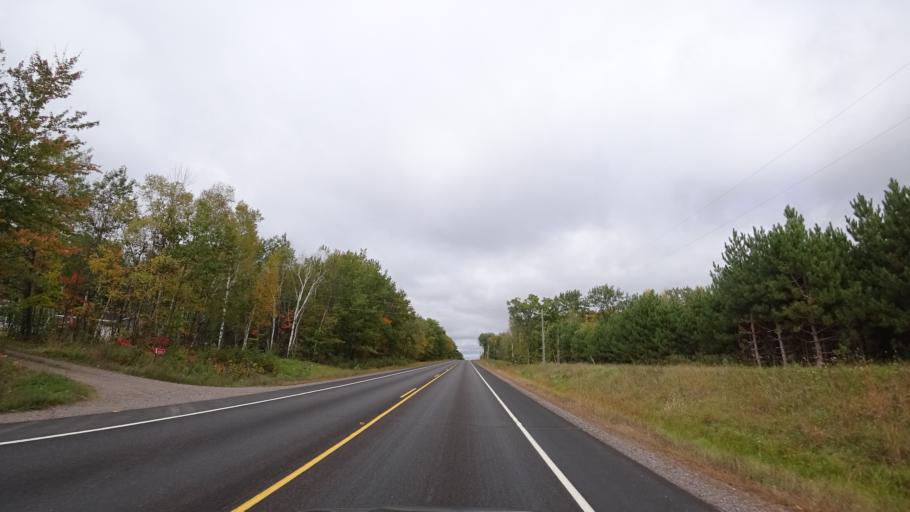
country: US
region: Wisconsin
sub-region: Rusk County
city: Ladysmith
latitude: 45.3388
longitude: -91.1110
